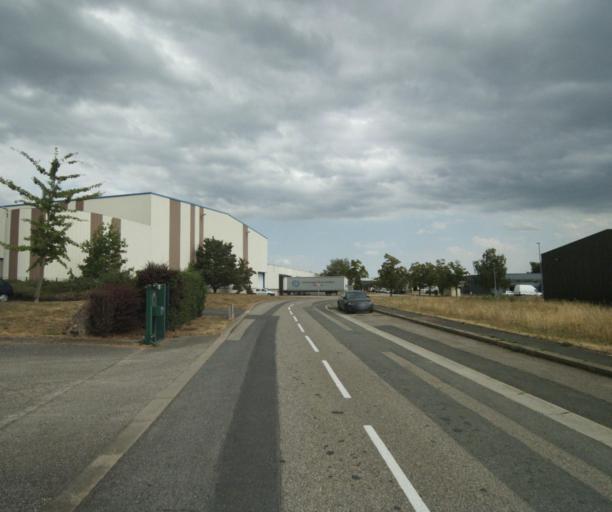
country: FR
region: Rhone-Alpes
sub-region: Departement du Rhone
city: Saint-Romain-de-Popey
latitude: 45.8792
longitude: 4.5419
